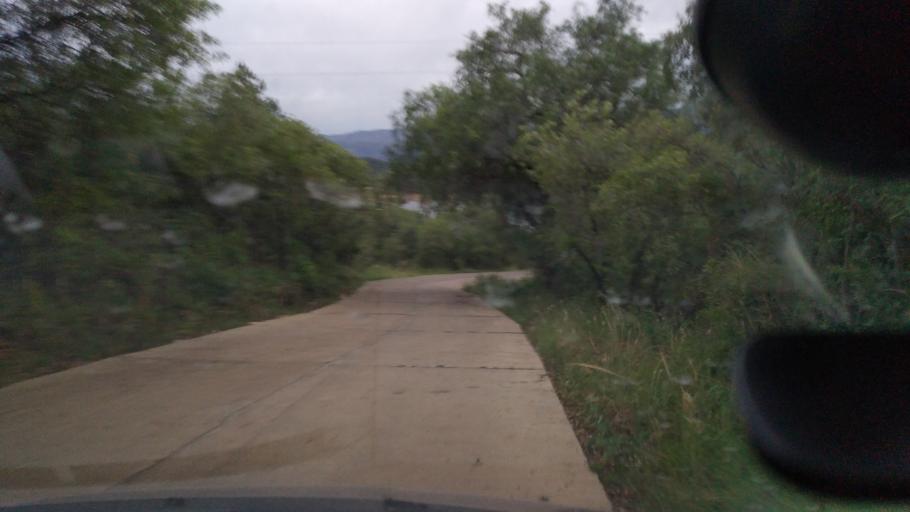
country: AR
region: Cordoba
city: Villa Las Rosas
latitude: -31.8783
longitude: -65.0241
